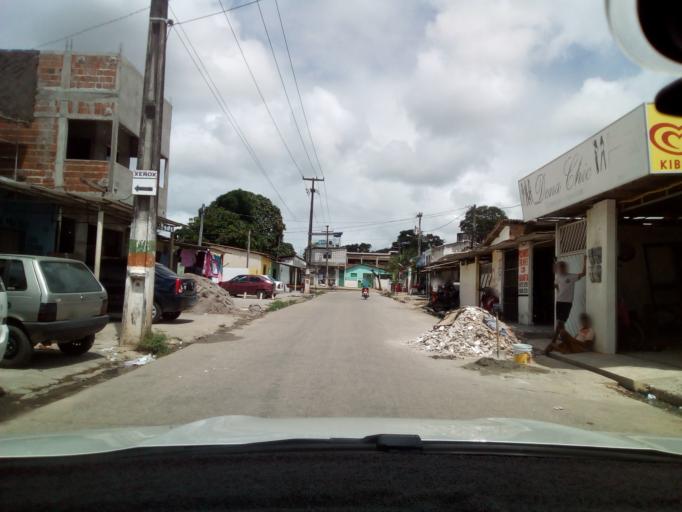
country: BR
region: Paraiba
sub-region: Bayeux
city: Bayeux
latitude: -7.1492
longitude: -34.9250
